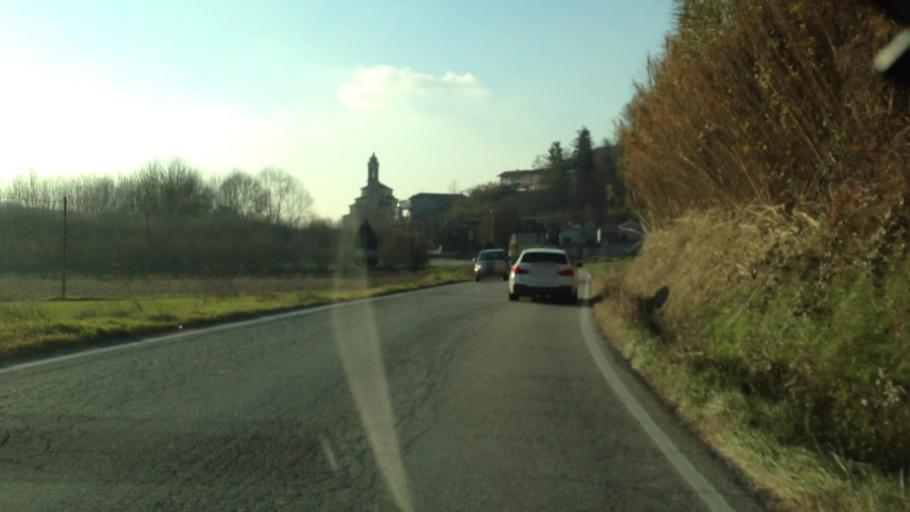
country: IT
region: Piedmont
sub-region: Provincia di Asti
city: Belveglio
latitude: 44.8308
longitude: 8.3362
